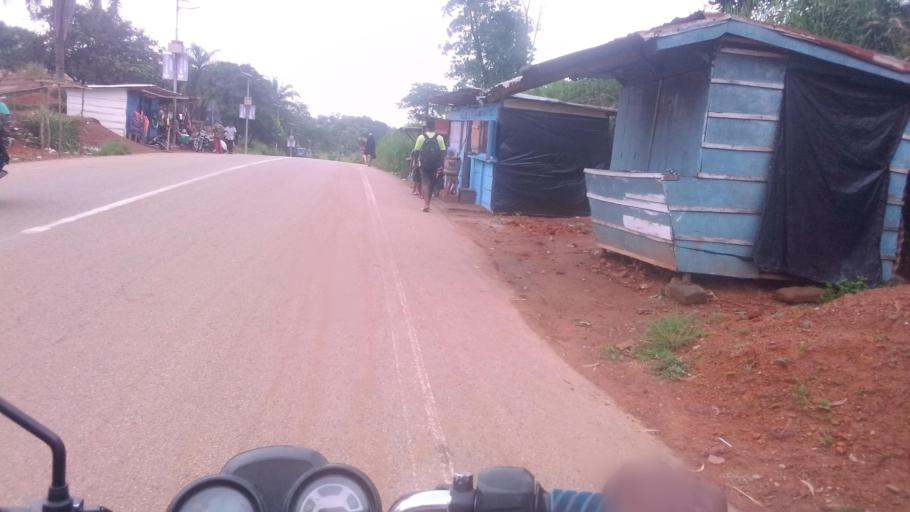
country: SL
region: Eastern Province
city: Kenema
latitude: 7.8761
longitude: -11.1776
